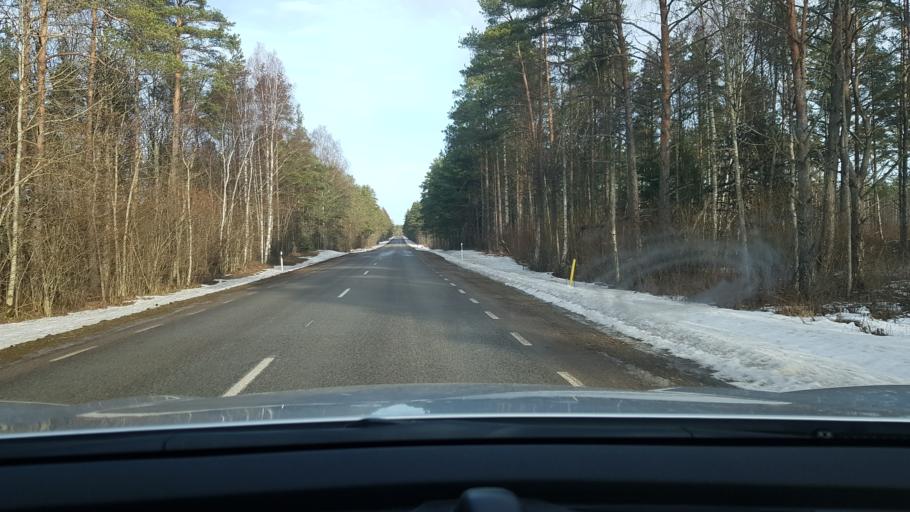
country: EE
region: Saare
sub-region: Kuressaare linn
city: Kuressaare
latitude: 58.4697
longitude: 22.7025
